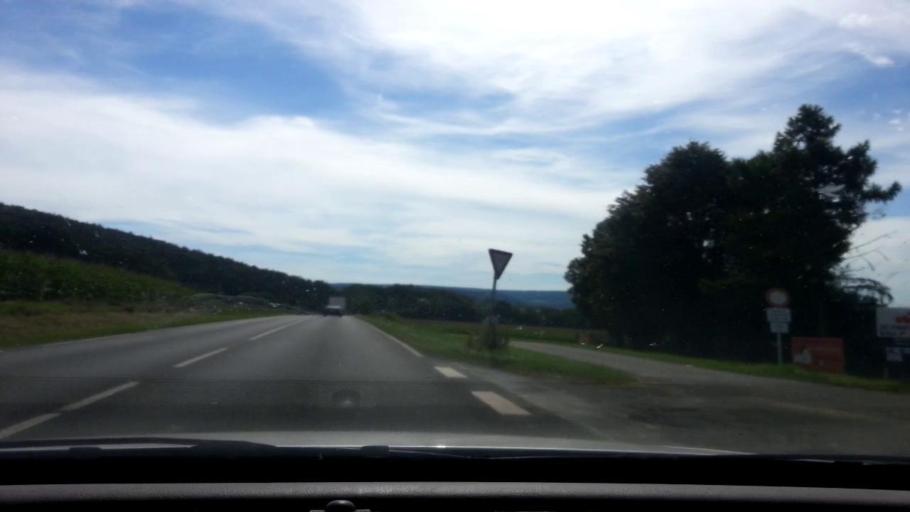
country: DE
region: Bavaria
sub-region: Upper Franconia
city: Gesees
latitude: 50.0490
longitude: 11.6395
